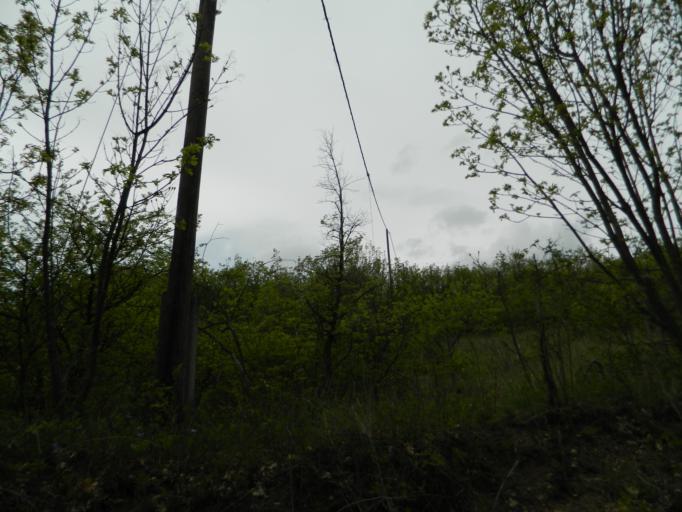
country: HU
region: Veszprem
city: Osi
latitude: 47.2159
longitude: 18.2167
